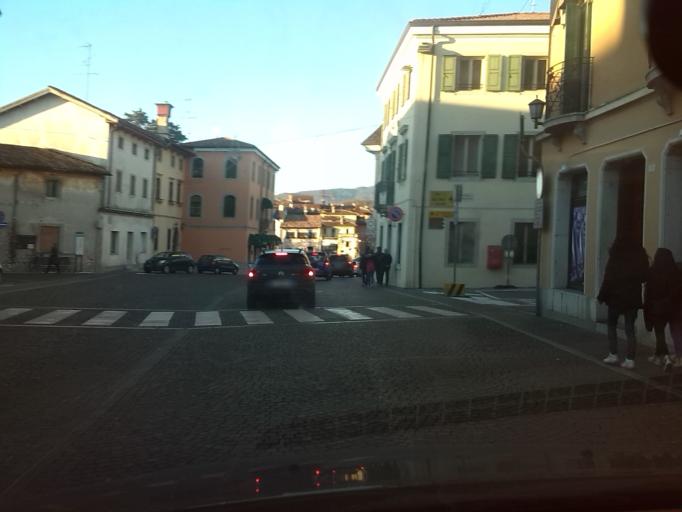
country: IT
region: Friuli Venezia Giulia
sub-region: Provincia di Udine
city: Cividale del Friuli
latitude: 46.0908
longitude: 13.4322
